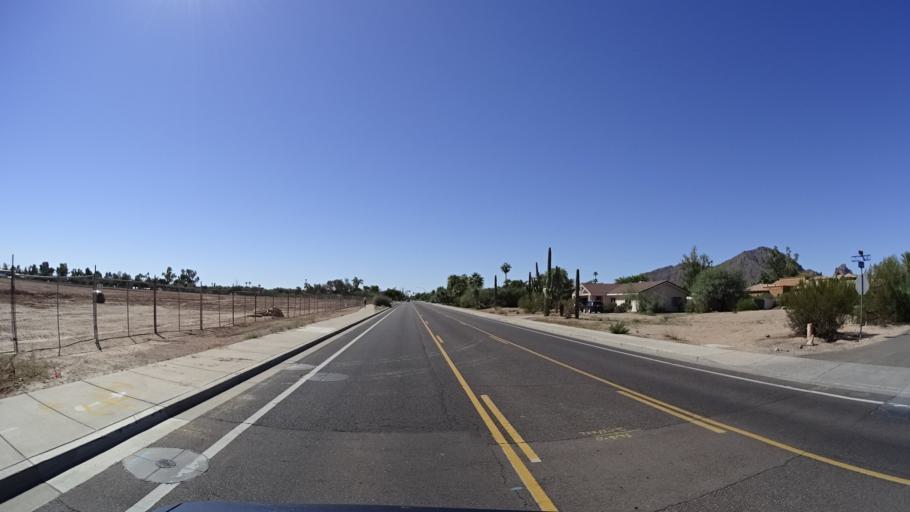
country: US
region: Arizona
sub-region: Maricopa County
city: Paradise Valley
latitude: 33.5339
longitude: -111.9344
